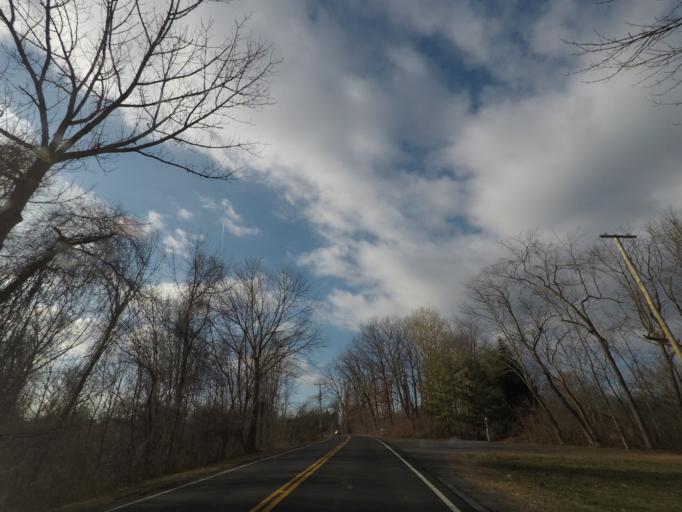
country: US
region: New York
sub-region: Albany County
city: Westmere
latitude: 42.6641
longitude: -73.8847
